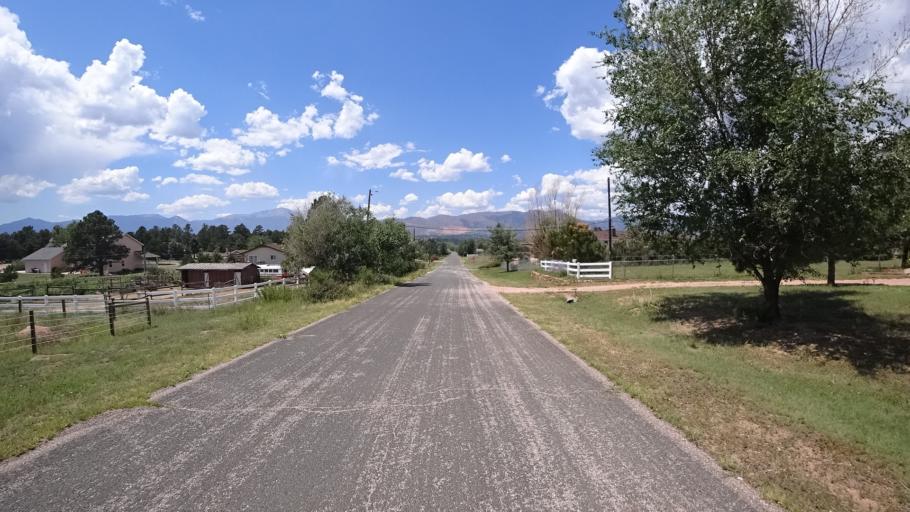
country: US
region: Colorado
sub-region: El Paso County
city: Air Force Academy
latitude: 38.9358
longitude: -104.8020
